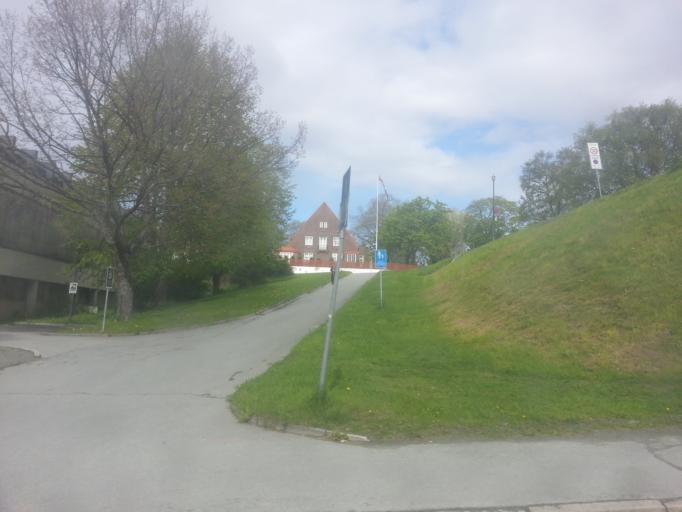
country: NO
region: Sor-Trondelag
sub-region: Trondheim
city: Trondheim
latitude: 63.4206
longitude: 10.4047
